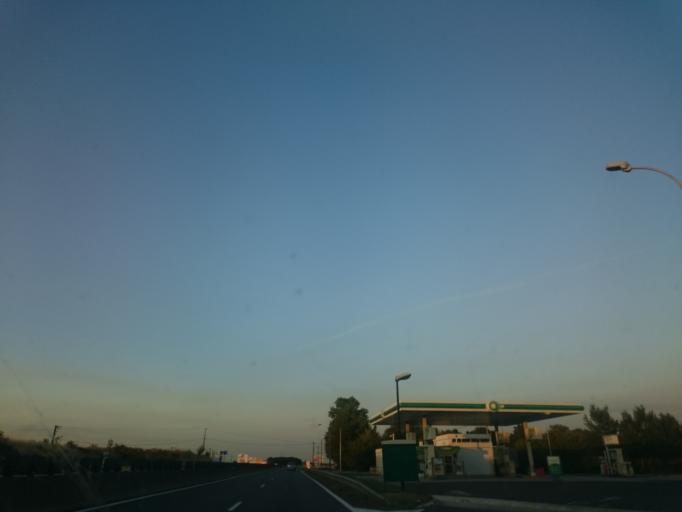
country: FR
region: Ile-de-France
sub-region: Departement de l'Essonne
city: Le Plessis-Pate
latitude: 48.6079
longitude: 2.3306
